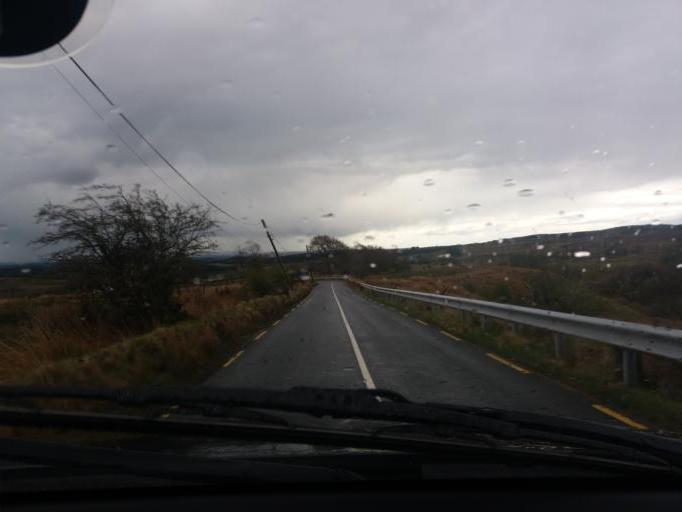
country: IE
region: Ulster
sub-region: An Cabhan
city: Ballyconnell
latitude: 54.1596
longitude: -7.7811
